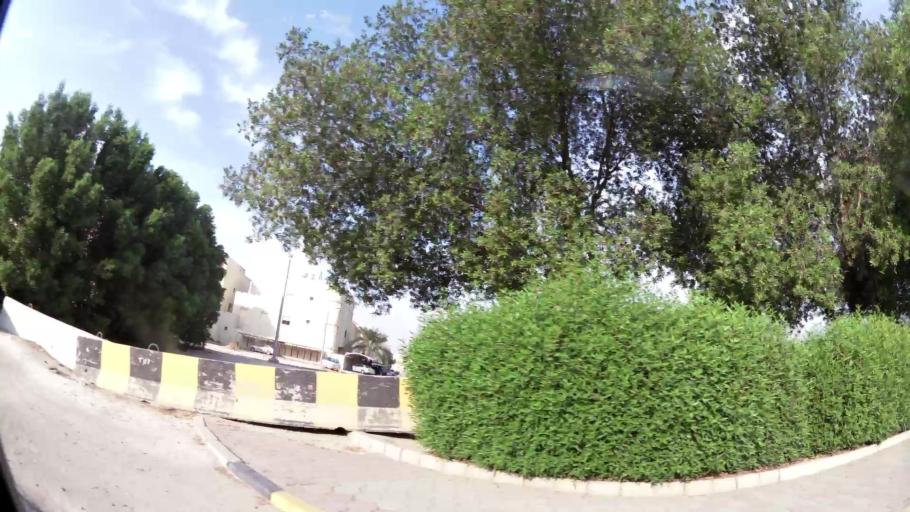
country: KW
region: Muhafazat Hawalli
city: Salwa
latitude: 29.3032
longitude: 48.0852
